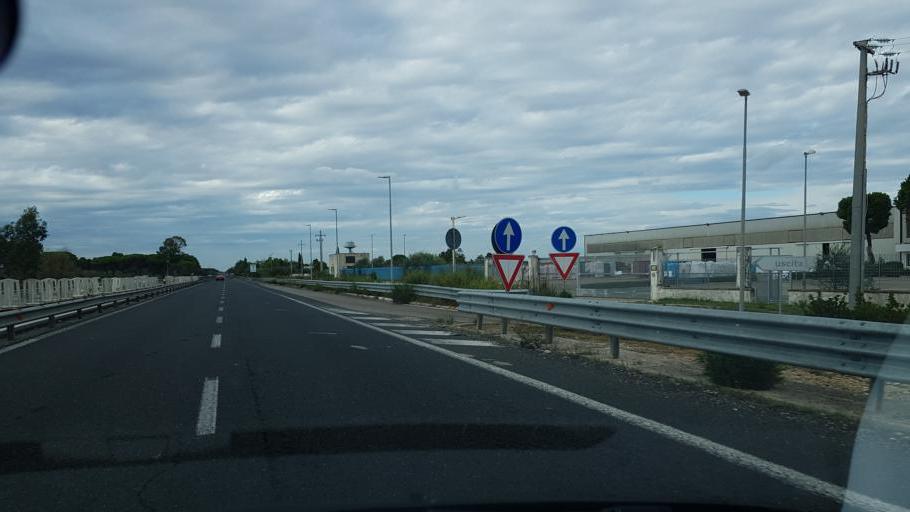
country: IT
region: Apulia
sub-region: Provincia di Lecce
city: San Donato di Lecce
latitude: 40.2807
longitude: 18.2018
